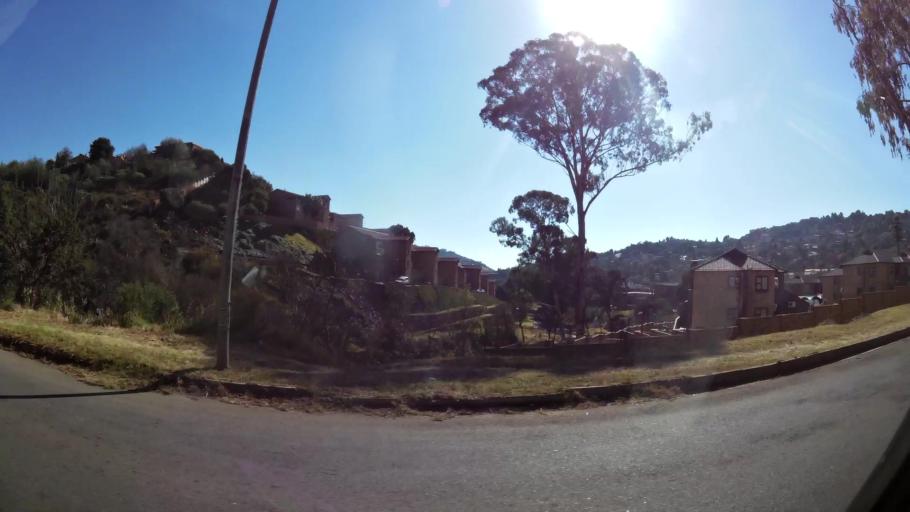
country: ZA
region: Gauteng
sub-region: City of Johannesburg Metropolitan Municipality
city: Roodepoort
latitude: -26.1248
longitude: 27.8732
